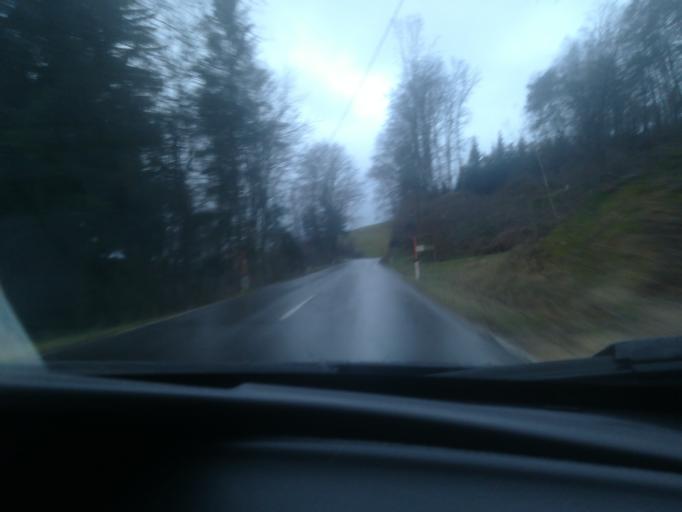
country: AT
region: Upper Austria
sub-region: Politischer Bezirk Perg
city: Perg
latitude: 48.2688
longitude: 14.6275
